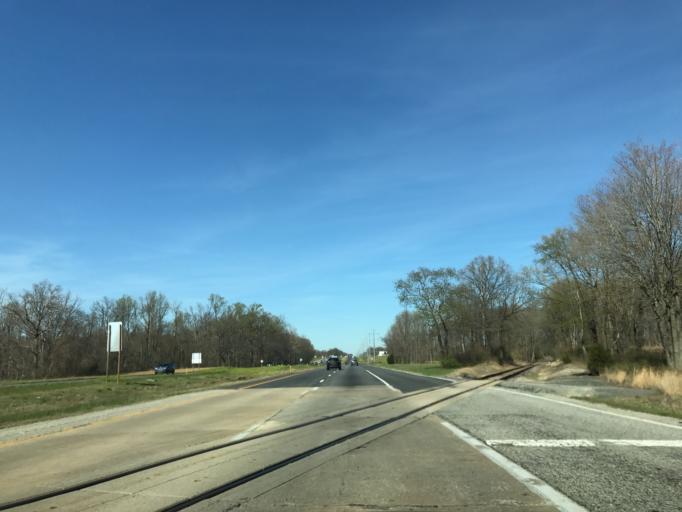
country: US
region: Maryland
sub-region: Queen Anne's County
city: Centreville
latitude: 39.0380
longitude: -76.0163
